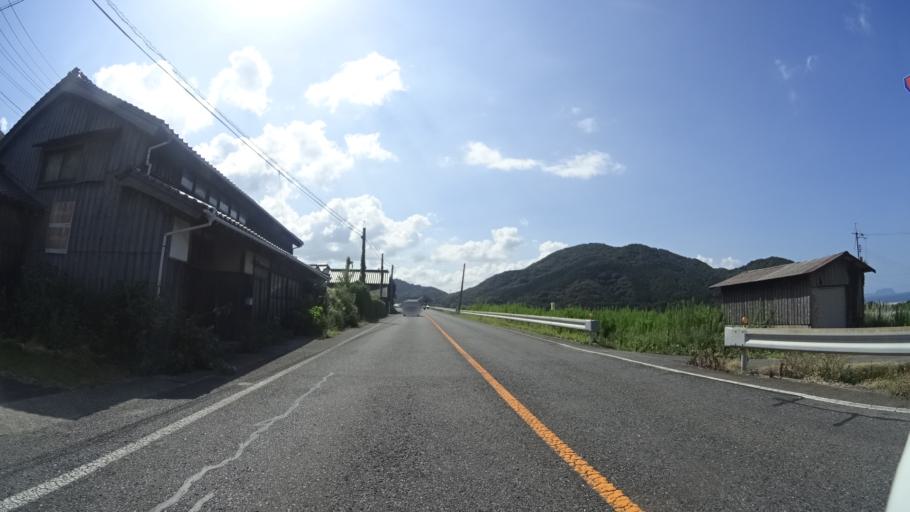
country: JP
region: Yamaguchi
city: Shimonoseki
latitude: 34.2308
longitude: 130.9260
